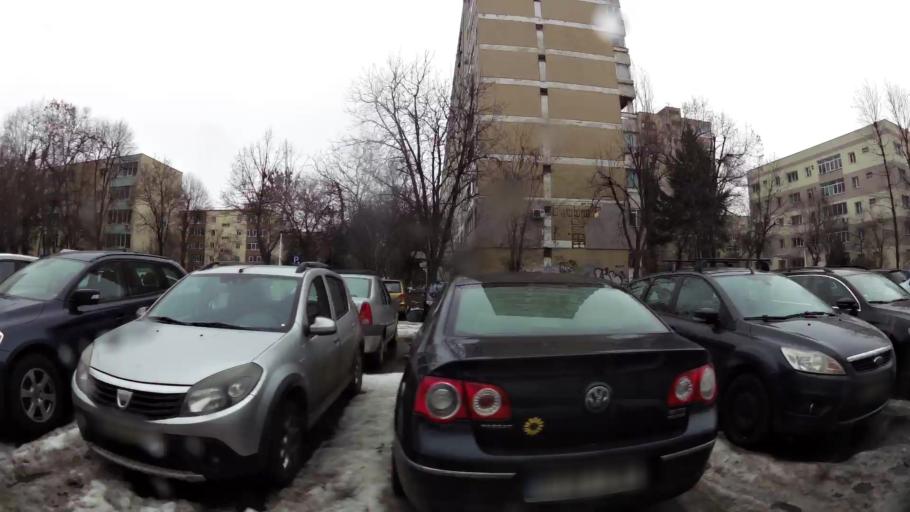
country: RO
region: Ilfov
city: Dobroesti
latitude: 44.4229
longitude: 26.1667
